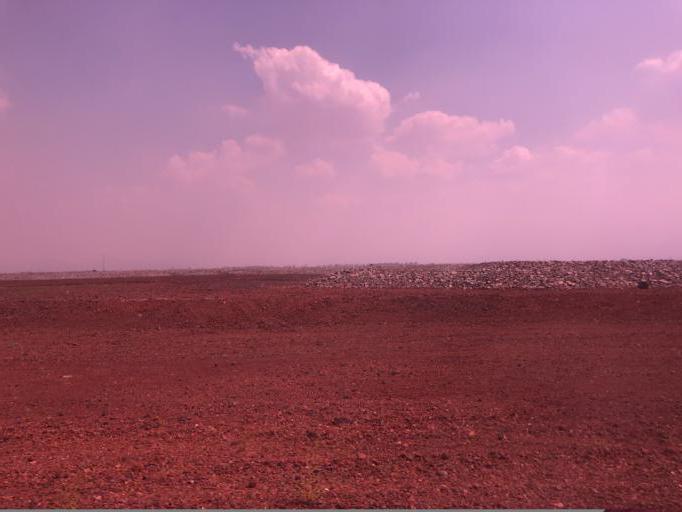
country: MX
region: Mexico
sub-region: Atenco
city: Colonia el Salado
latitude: 19.5476
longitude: -98.9939
